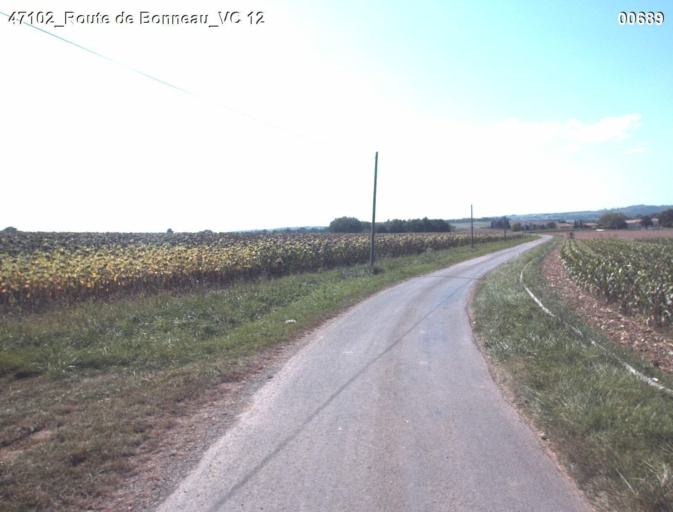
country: FR
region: Aquitaine
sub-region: Departement du Lot-et-Garonne
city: Nerac
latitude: 44.0824
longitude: 0.4095
